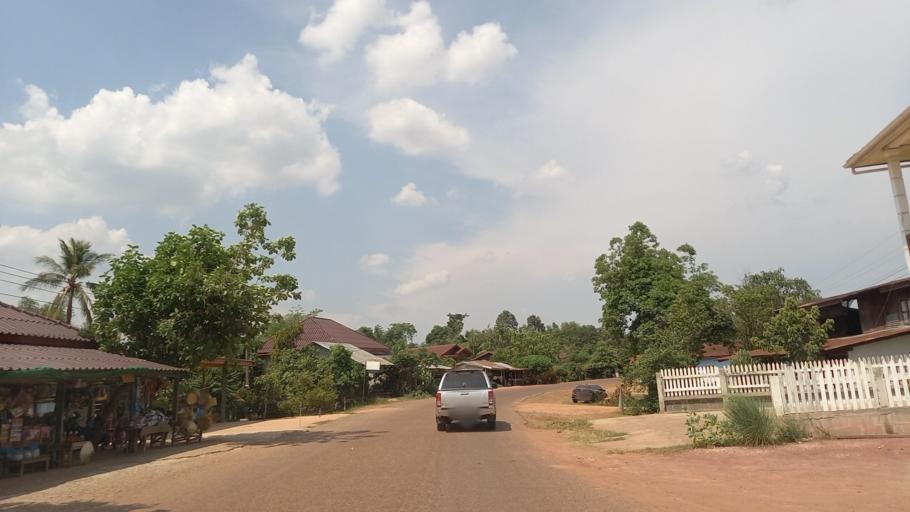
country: LA
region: Bolikhamxai
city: Muang Pakxan
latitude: 18.4279
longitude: 103.7120
